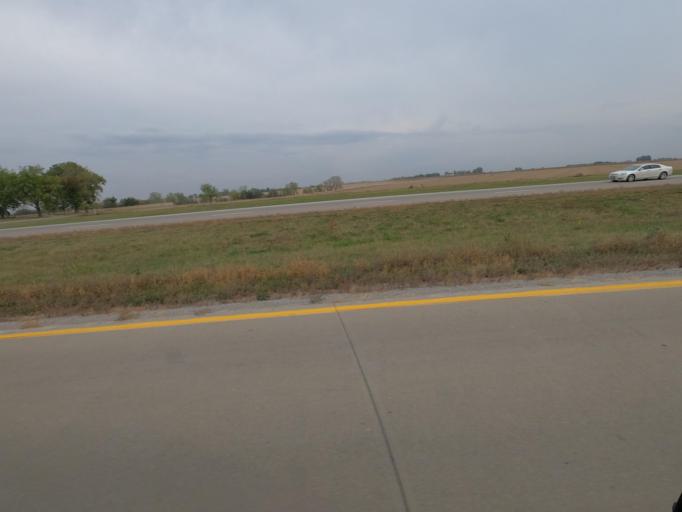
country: US
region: Iowa
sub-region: Marion County
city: Pella
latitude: 41.3836
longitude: -92.8226
